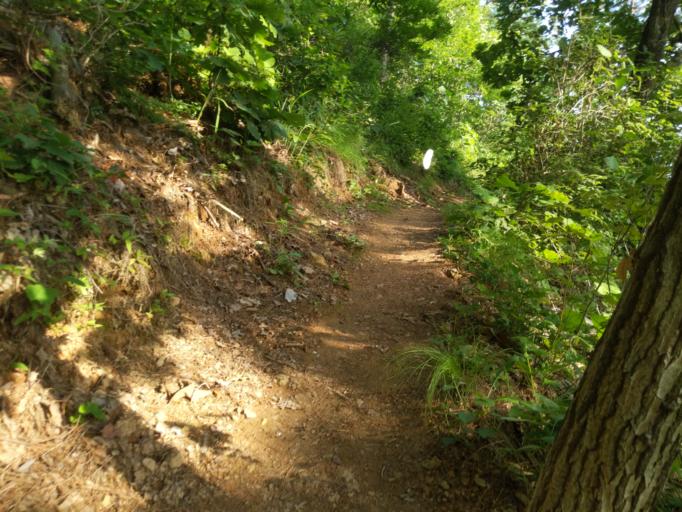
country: KR
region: Daegu
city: Hwawon
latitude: 35.7884
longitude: 128.5405
